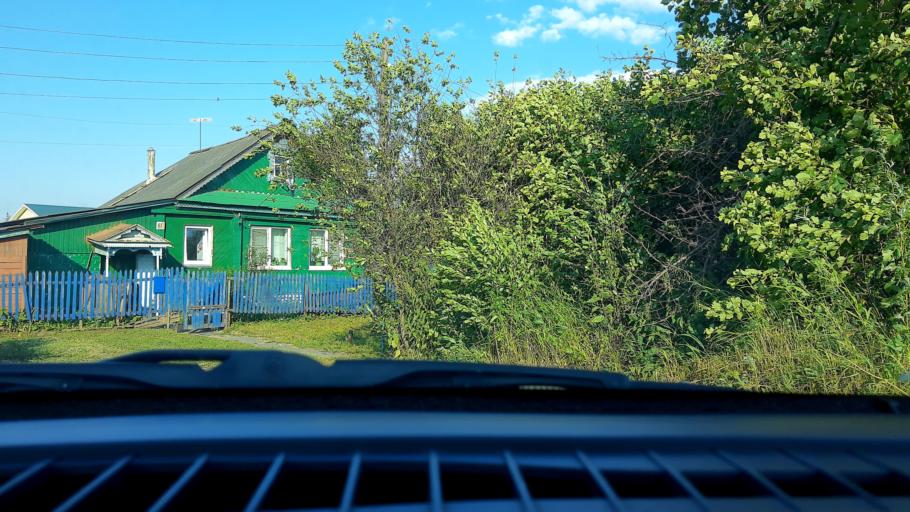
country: RU
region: Nizjnij Novgorod
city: Bor
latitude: 56.3729
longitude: 44.0638
